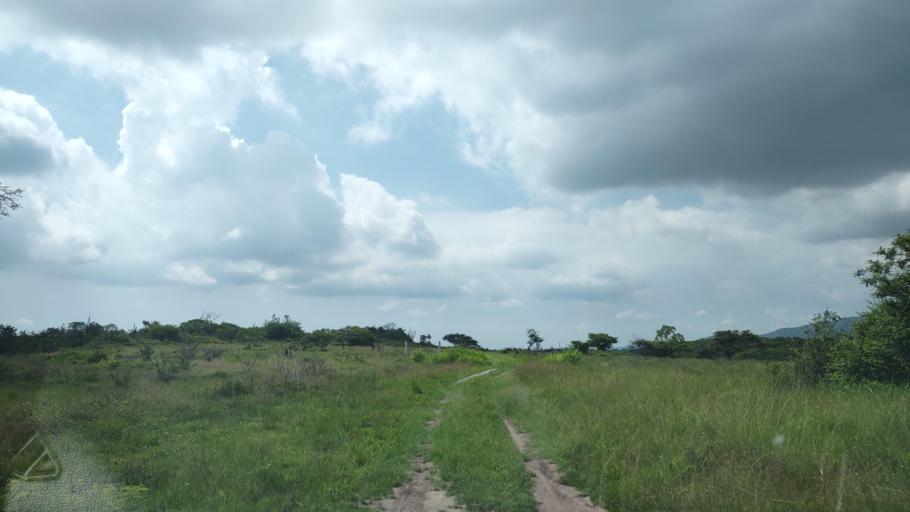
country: MX
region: Veracruz
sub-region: Emiliano Zapata
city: Dos Rios
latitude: 19.4598
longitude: -96.7937
